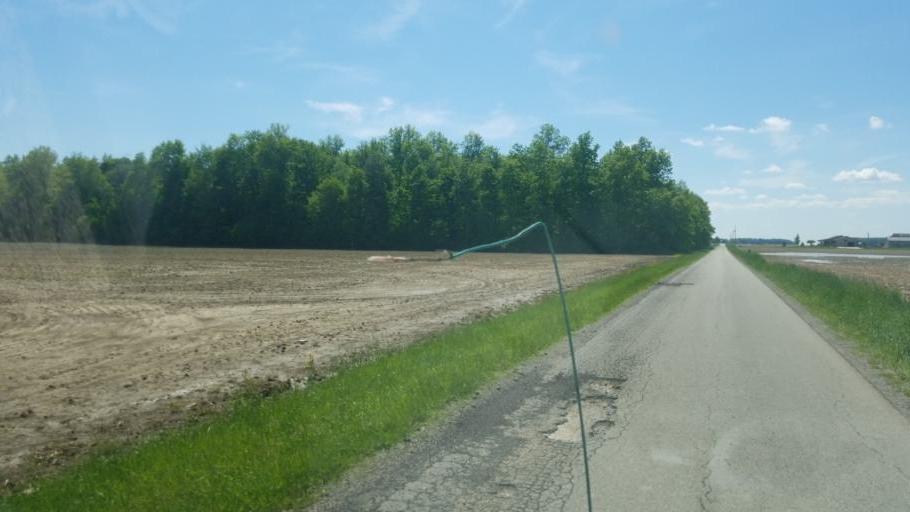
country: US
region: Ohio
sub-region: Crawford County
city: Bucyrus
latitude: 40.9795
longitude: -83.0051
